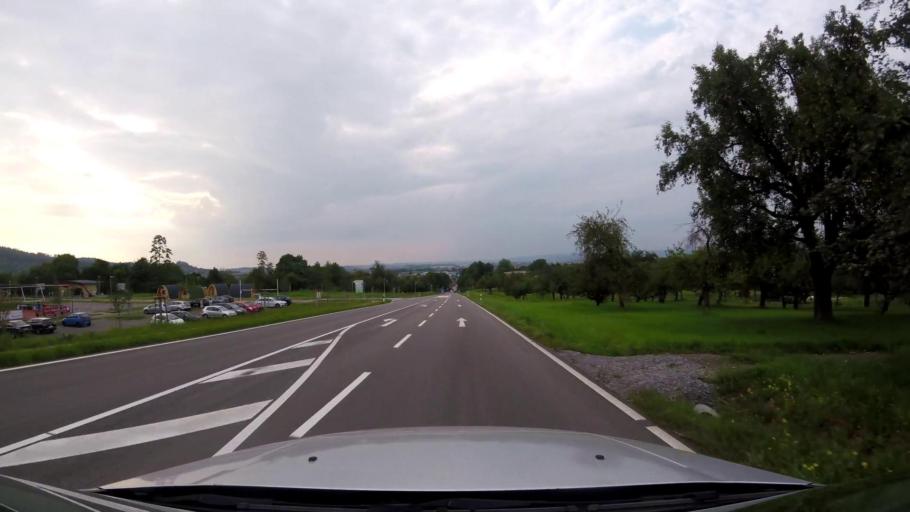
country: DE
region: Baden-Wuerttemberg
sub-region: Regierungsbezirk Stuttgart
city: Allmersbach im Tal
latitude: 48.9017
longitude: 9.4772
